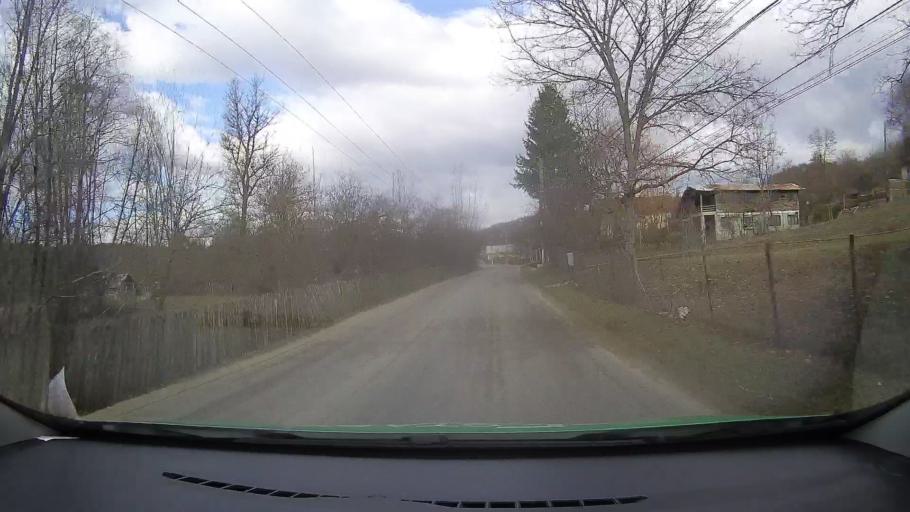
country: RO
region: Prahova
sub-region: Comuna Provita de Jos
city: Provita de Jos
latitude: 45.1262
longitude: 25.6526
